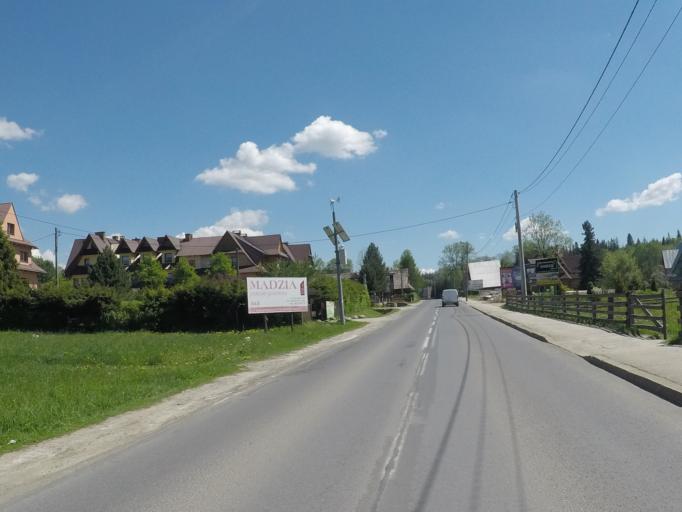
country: PL
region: Lesser Poland Voivodeship
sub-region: Powiat tatrzanski
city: Poronin
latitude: 49.3335
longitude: 20.0105
